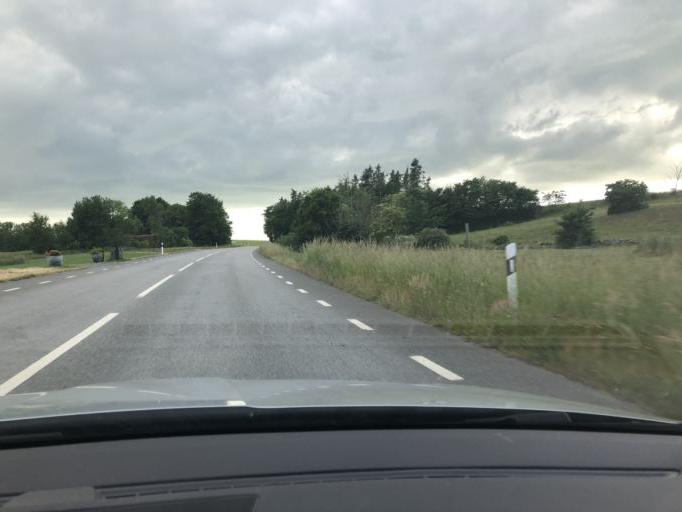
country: SE
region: Skane
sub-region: Simrishamns Kommun
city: Simrishamn
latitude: 55.5316
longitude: 14.2691
